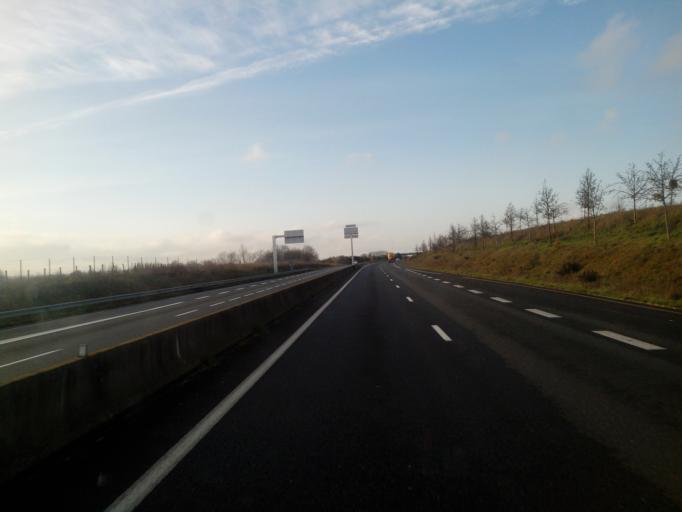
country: FR
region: Poitou-Charentes
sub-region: Departement des Deux-Sevres
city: Saint-Pierre-des-Echaubrognes
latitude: 46.9305
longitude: -0.7310
